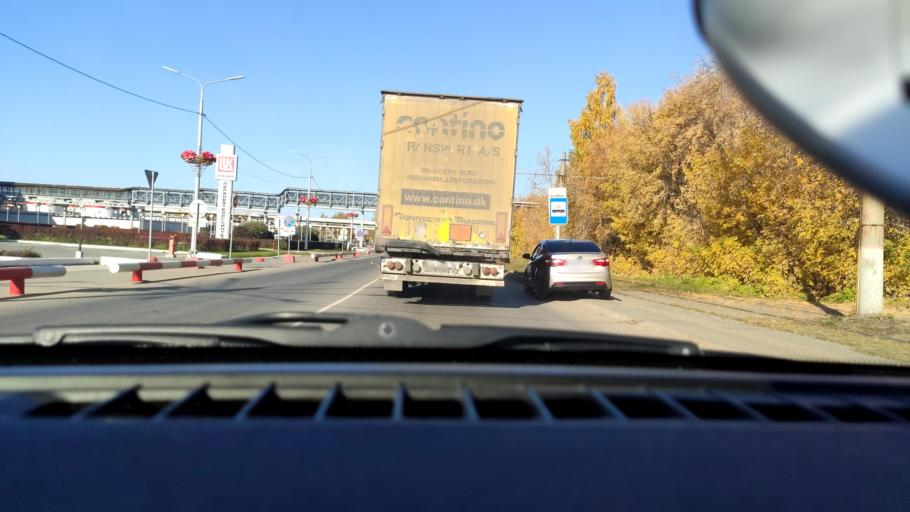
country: RU
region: Perm
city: Kondratovo
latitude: 57.9234
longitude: 56.1403
